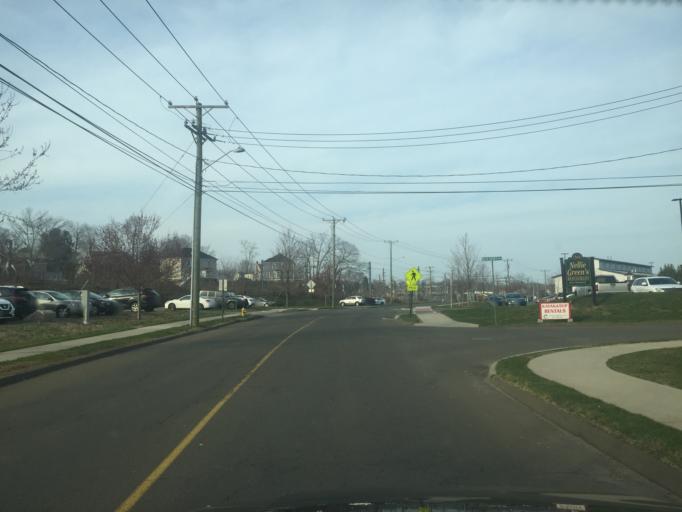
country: US
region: Connecticut
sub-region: New Haven County
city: Branford Center
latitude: 41.2738
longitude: -72.8159
